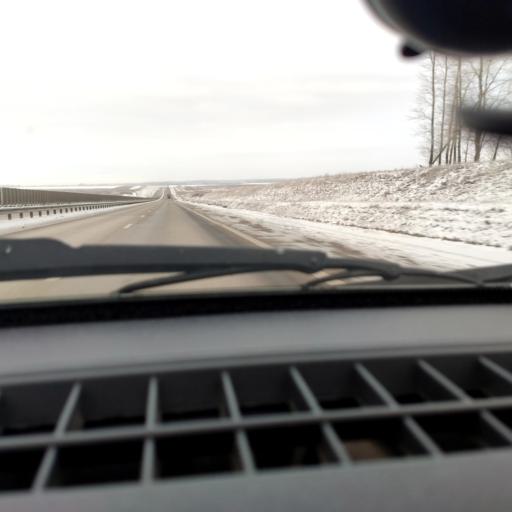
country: RU
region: Bashkortostan
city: Kushnarenkovo
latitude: 55.1005
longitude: 55.2406
